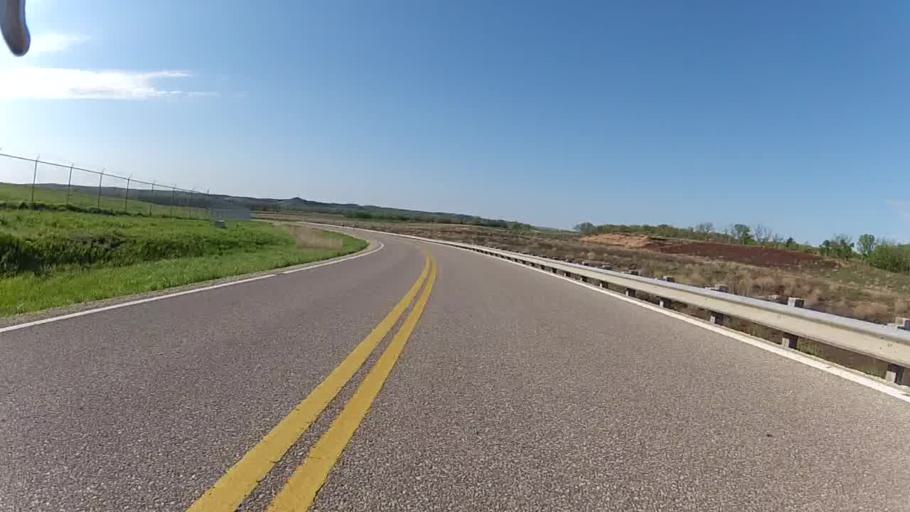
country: US
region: Kansas
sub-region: Riley County
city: Ogden
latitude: 39.1289
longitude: -96.6881
